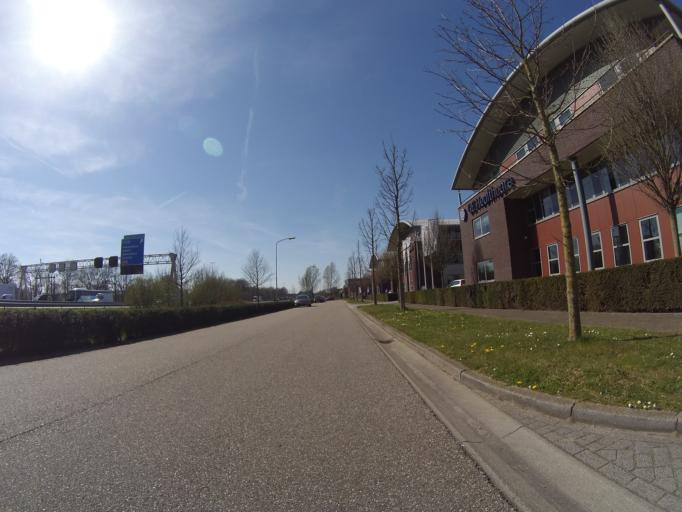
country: NL
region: Gelderland
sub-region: Gemeente Barneveld
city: Zwartebroek
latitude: 52.1667
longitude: 5.4651
